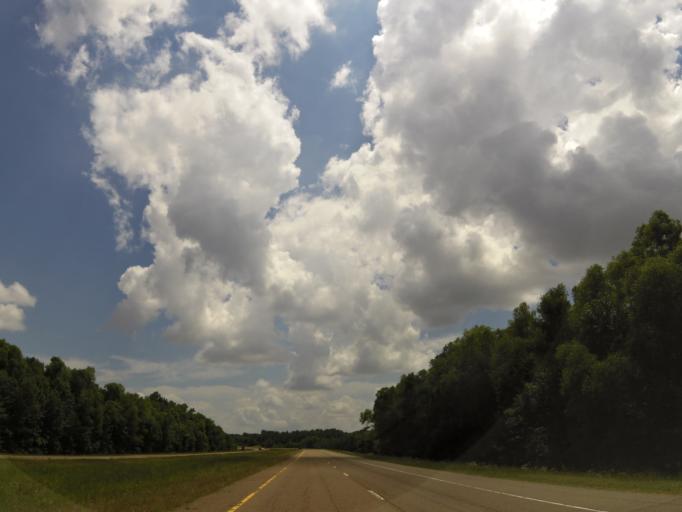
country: US
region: Tennessee
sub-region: Dyer County
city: Dyersburg
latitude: 35.9864
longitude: -89.3428
